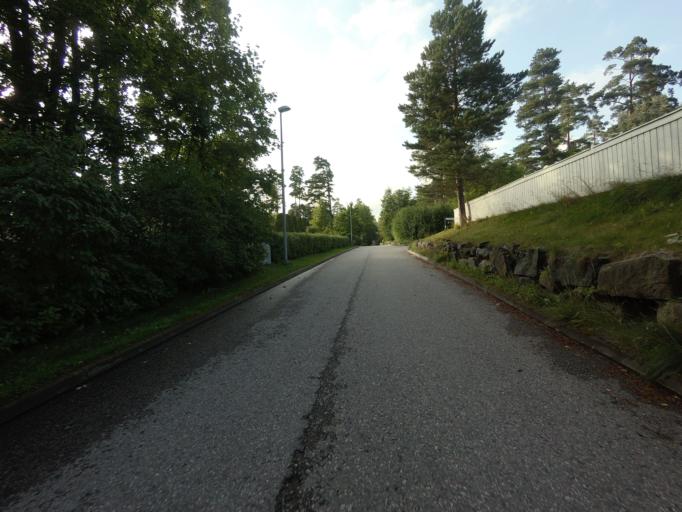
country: FI
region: Uusimaa
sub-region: Helsinki
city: Espoo
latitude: 60.1580
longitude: 24.6688
